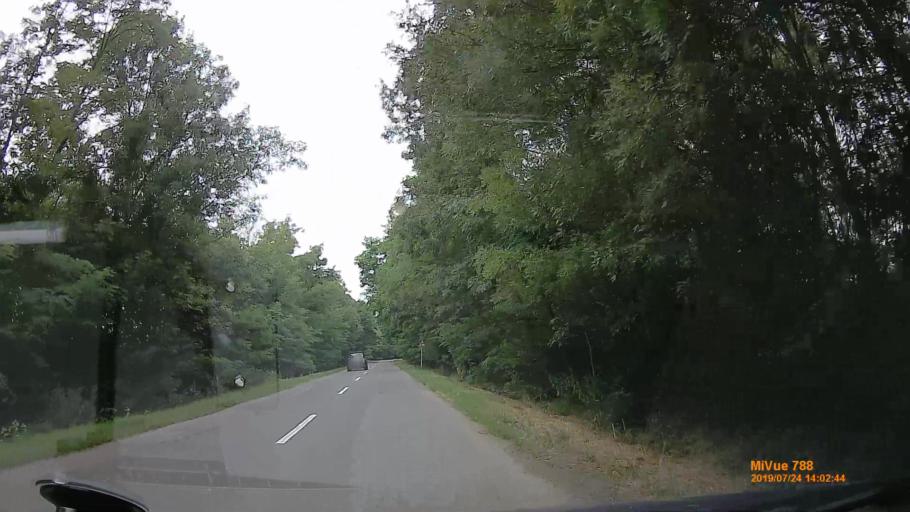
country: HU
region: Szabolcs-Szatmar-Bereg
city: Aranyosapati
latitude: 48.2710
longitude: 22.2855
